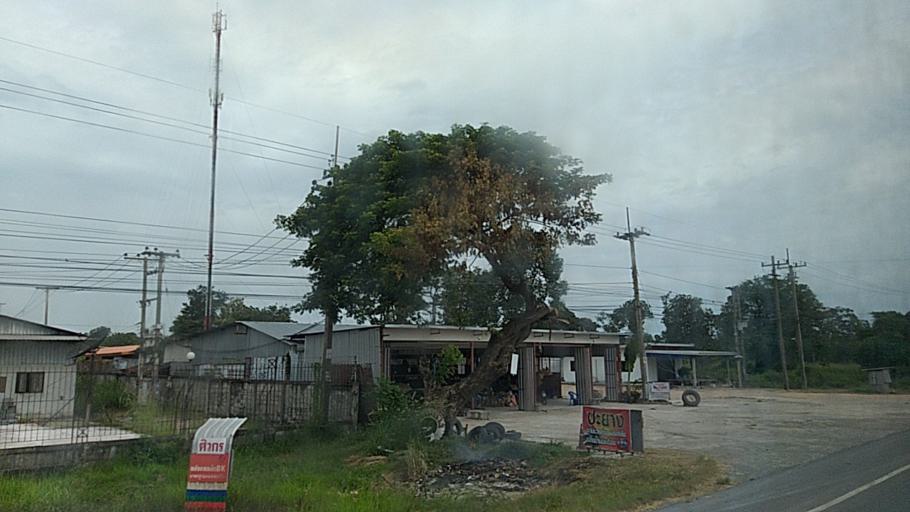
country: TH
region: Roi Et
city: Changhan
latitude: 16.0804
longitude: 103.5767
